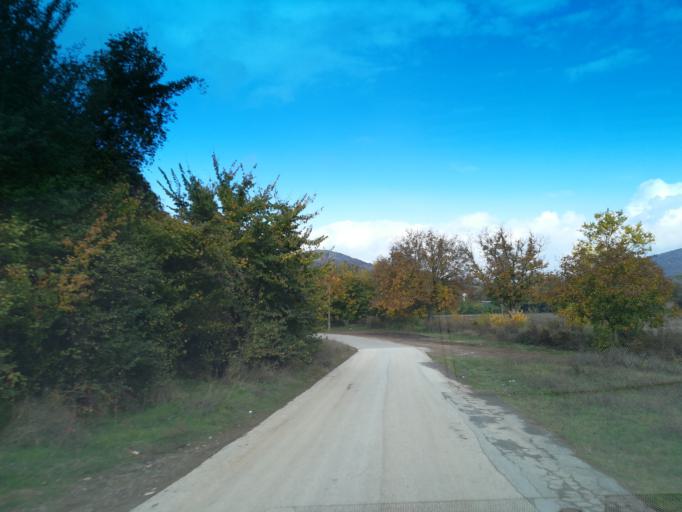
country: BG
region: Stara Zagora
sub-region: Obshtina Nikolaevo
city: Elkhovo
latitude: 42.3380
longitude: 25.4066
